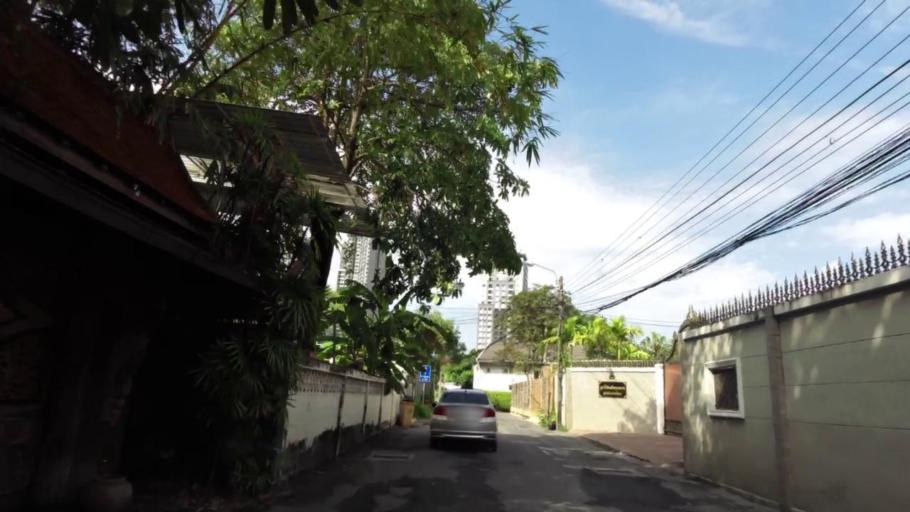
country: TH
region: Bangkok
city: Phra Khanong
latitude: 13.7167
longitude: 100.6005
